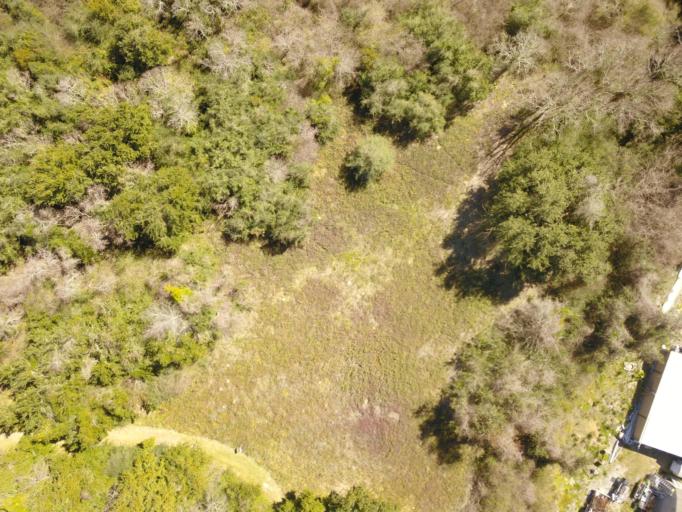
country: US
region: Texas
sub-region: Galveston County
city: Bolivar Peninsula
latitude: 29.5595
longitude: -94.3903
